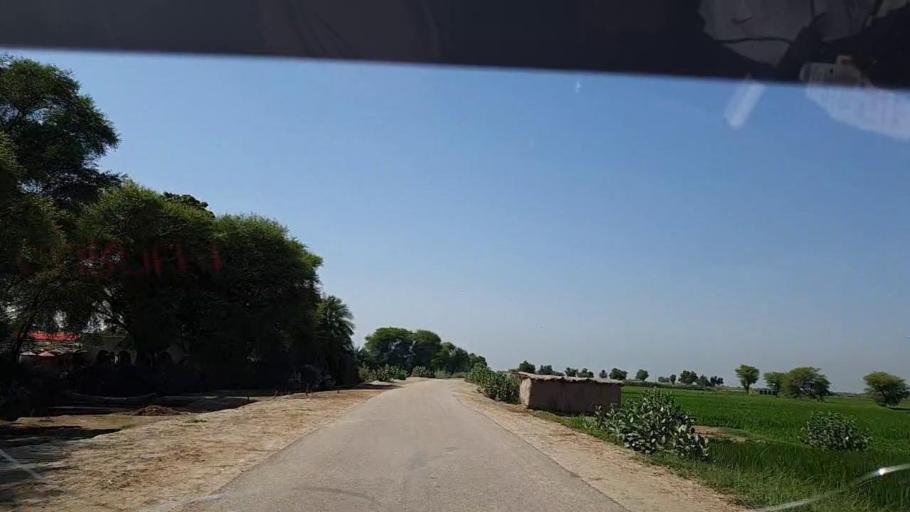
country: PK
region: Sindh
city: Kandhkot
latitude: 28.3056
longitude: 69.1108
